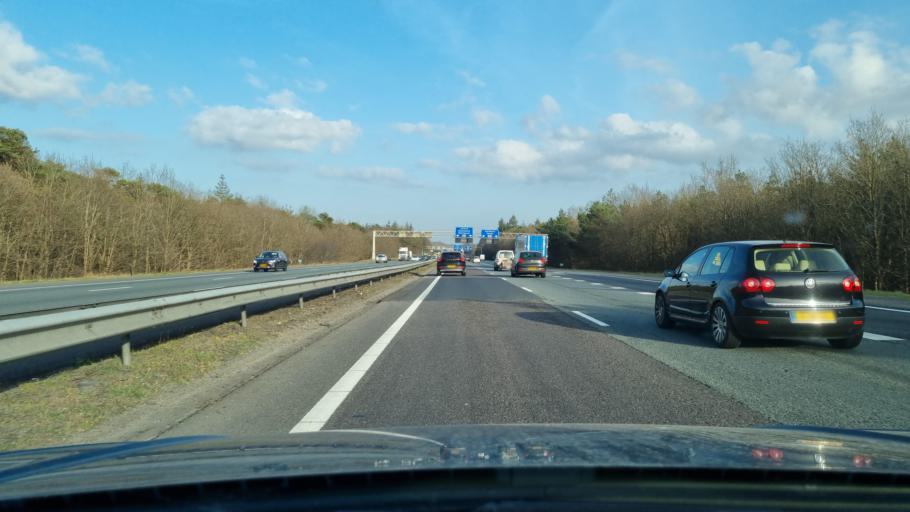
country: NL
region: Gelderland
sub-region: Gemeente Arnhem
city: Gulden Bodem
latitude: 52.0231
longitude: 5.8988
